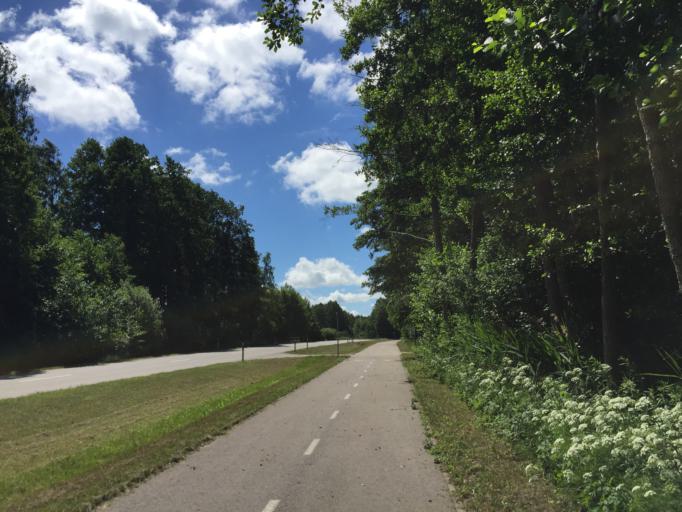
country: LV
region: Ventspils
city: Ventspils
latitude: 57.4325
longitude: 21.6522
